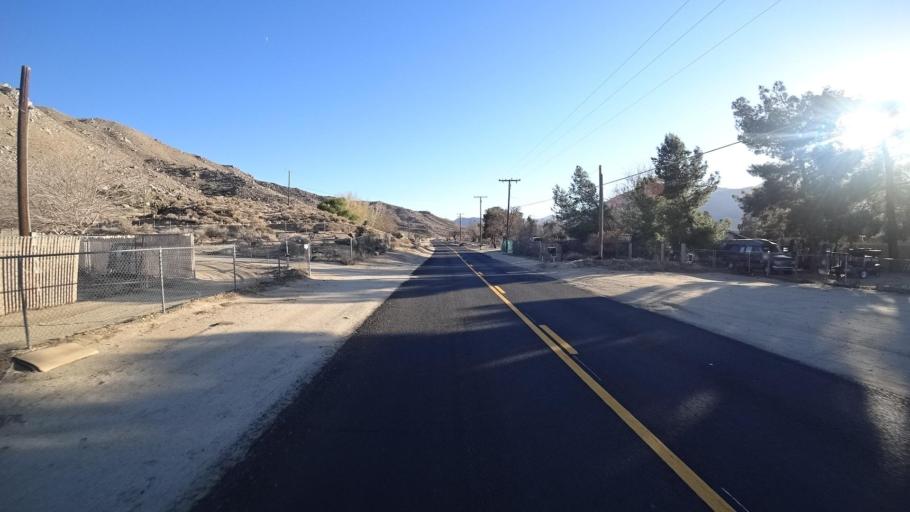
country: US
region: California
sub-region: Kern County
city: Weldon
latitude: 35.6329
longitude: -118.2438
